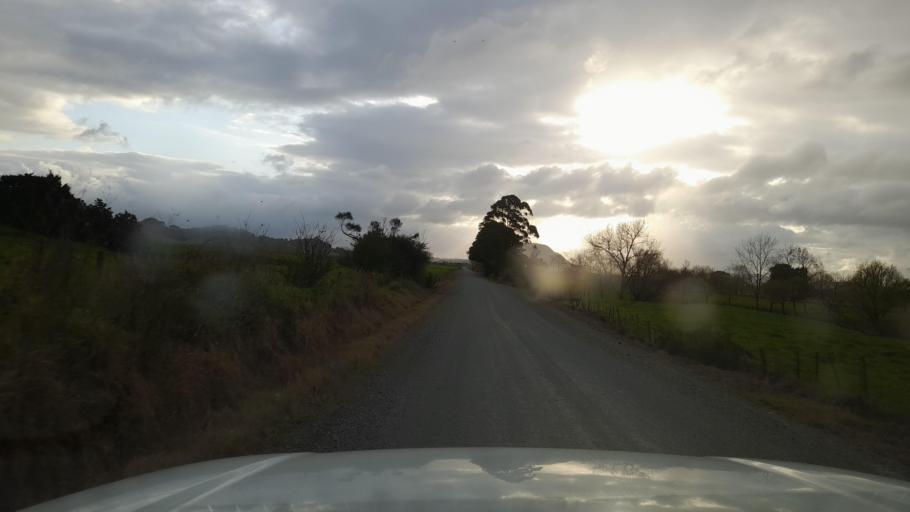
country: NZ
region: Northland
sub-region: Whangarei
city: Maungatapere
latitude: -35.6159
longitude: 174.1997
